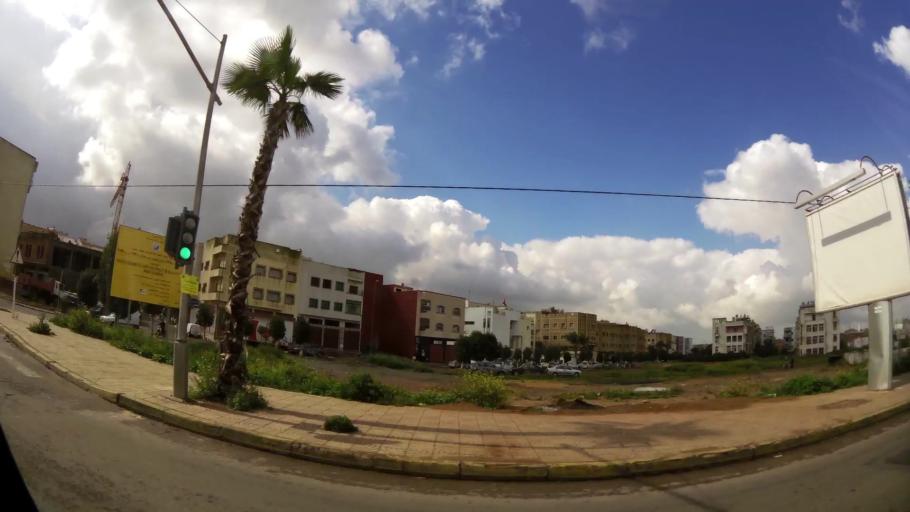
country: MA
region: Grand Casablanca
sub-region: Mediouna
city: Tit Mellil
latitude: 33.5535
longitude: -7.4760
